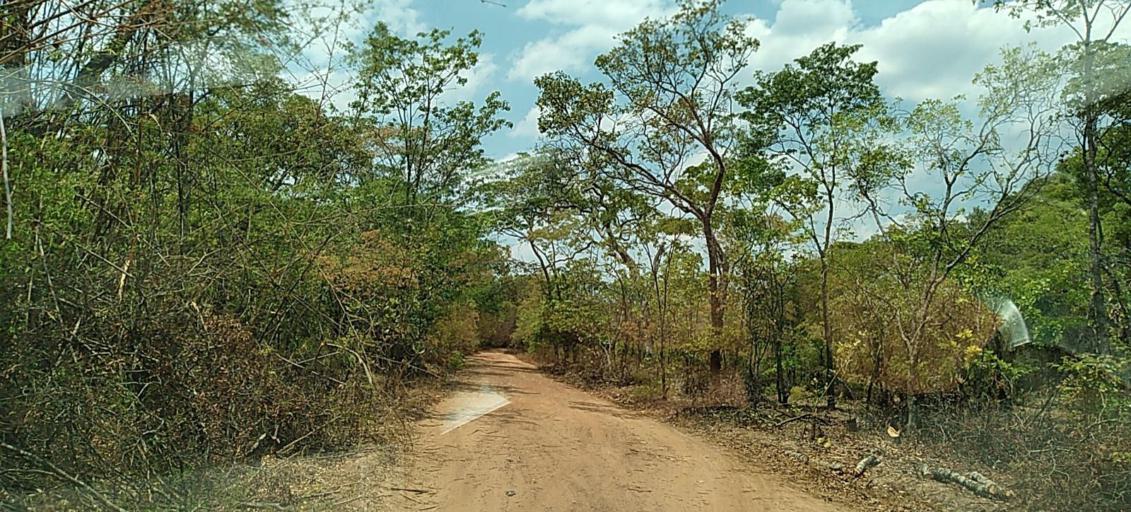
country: ZM
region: Copperbelt
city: Chililabombwe
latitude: -12.5144
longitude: 27.6278
